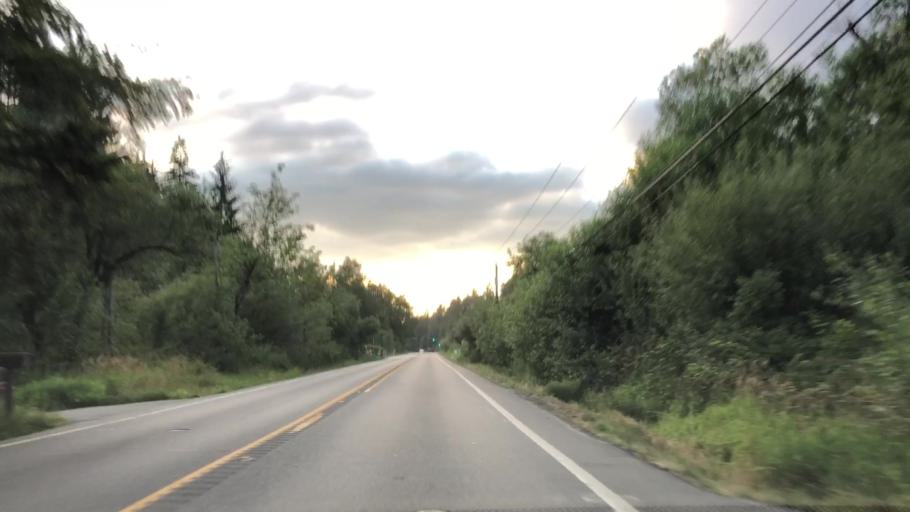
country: US
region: Washington
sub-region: King County
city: Ames Lake
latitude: 47.6379
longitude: -122.0058
